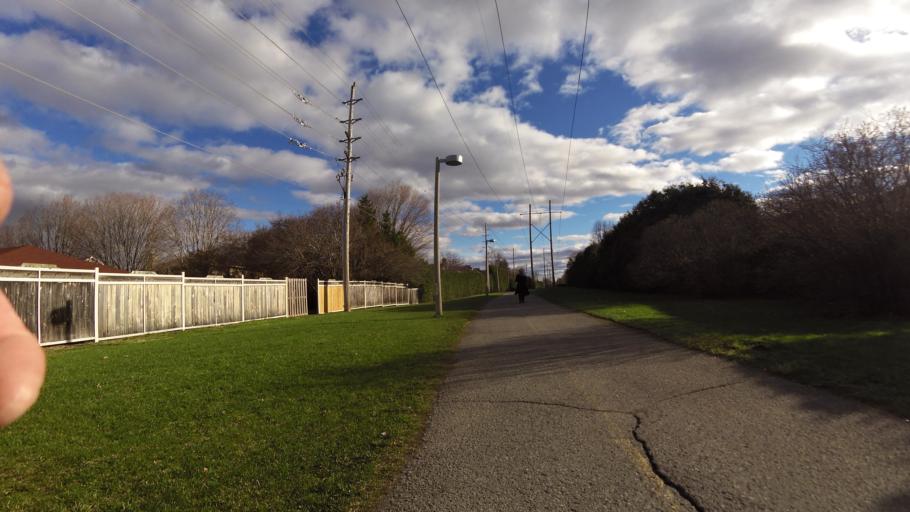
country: CA
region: Ontario
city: Bells Corners
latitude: 45.3392
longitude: -75.7720
